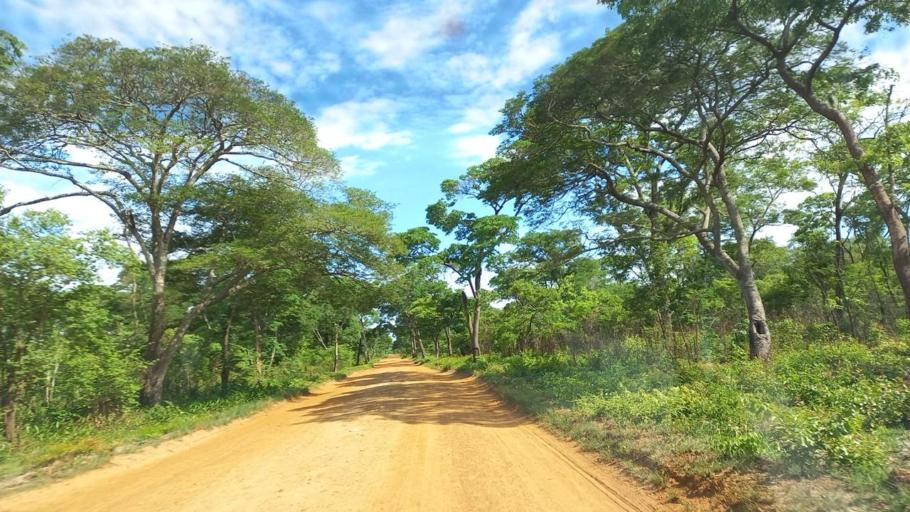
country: ZM
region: North-Western
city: Kabompo
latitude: -13.0833
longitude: 24.2202
